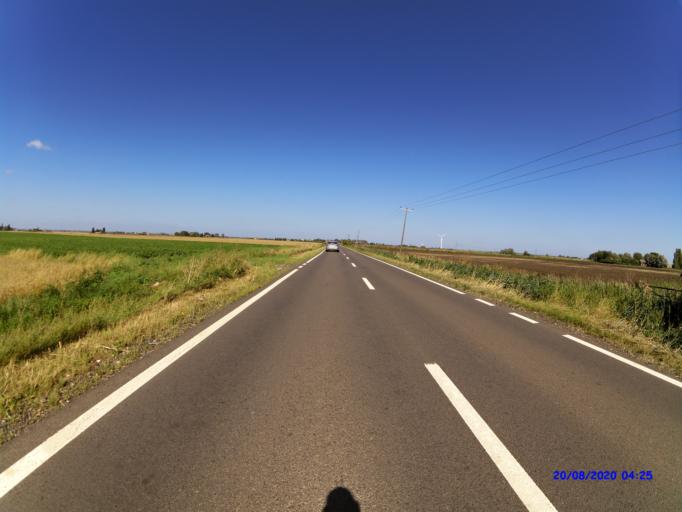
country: GB
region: England
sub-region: Cambridgeshire
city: Whittlesey
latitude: 52.5013
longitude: -0.1299
